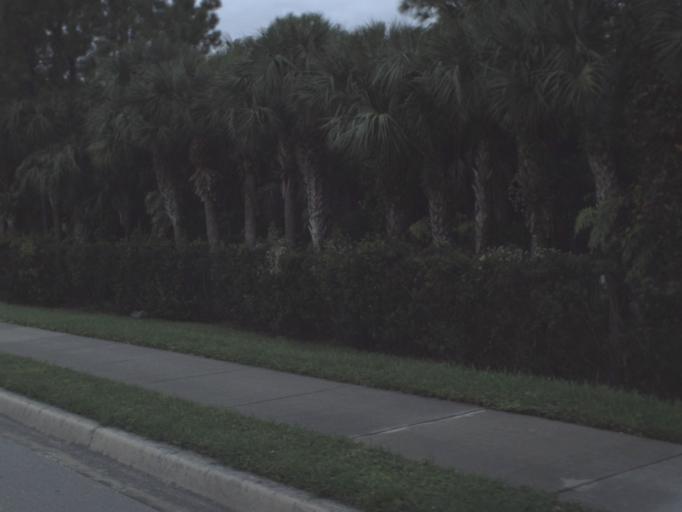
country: US
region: Florida
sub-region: Collier County
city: Golden Gate
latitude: 26.1409
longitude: -81.6869
